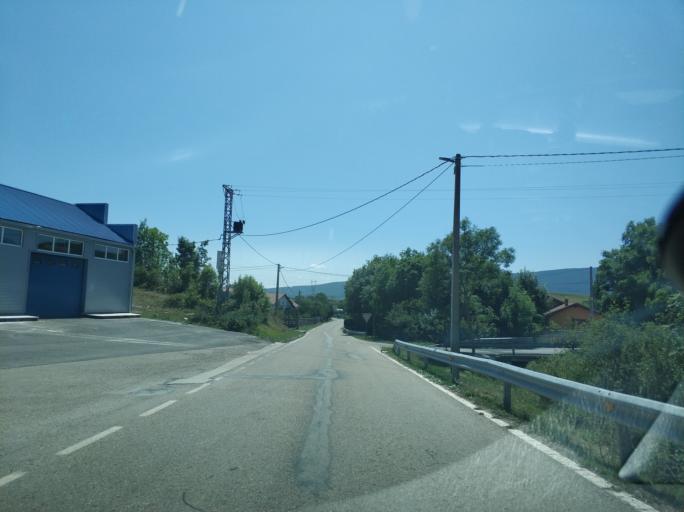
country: ES
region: Cantabria
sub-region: Provincia de Cantabria
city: Reinosa
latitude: 43.0095
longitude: -4.1667
